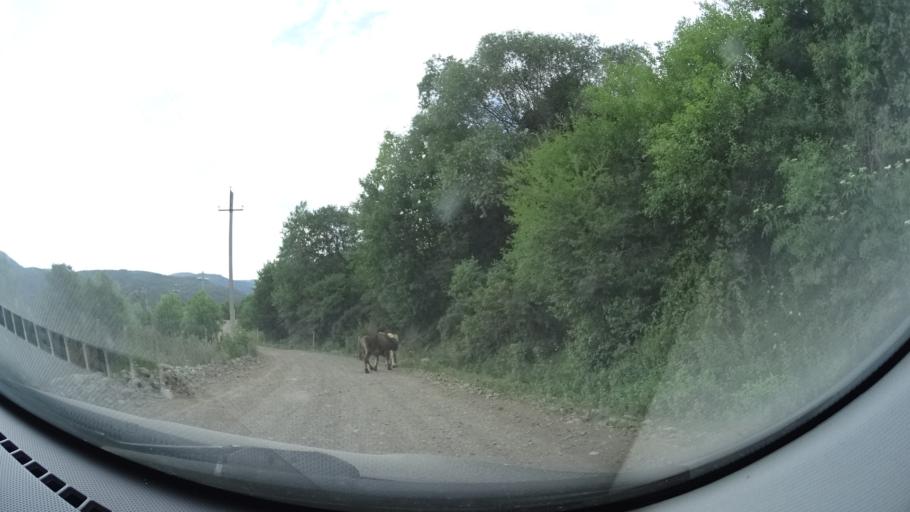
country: GE
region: Samtskhe-Javakheti
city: Adigeni
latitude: 41.6761
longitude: 42.6460
